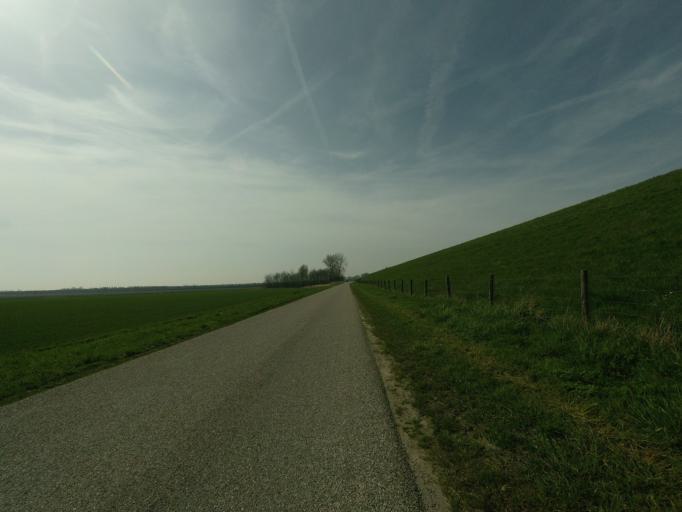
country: NL
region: Zeeland
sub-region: Gemeente Hulst
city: Hulst
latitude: 51.3648
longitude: 4.0615
